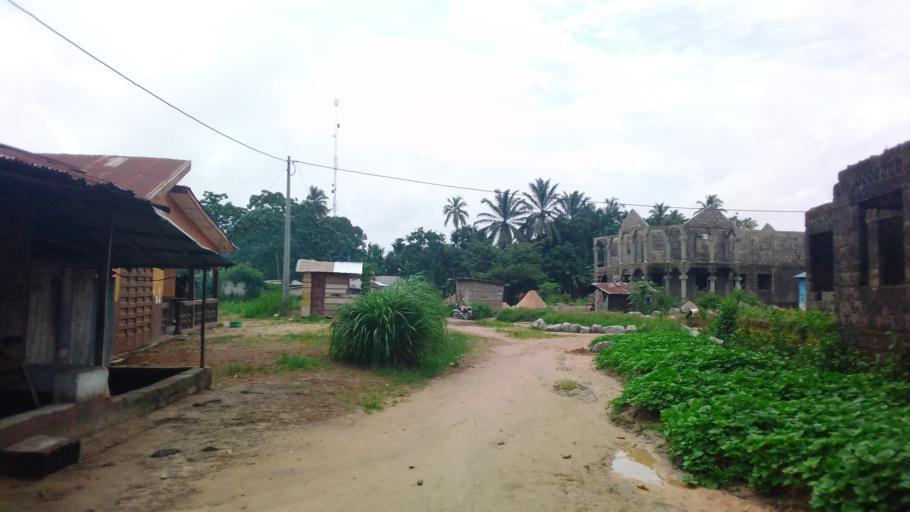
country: SL
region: Northern Province
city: Lunsar
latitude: 8.6836
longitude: -12.5395
